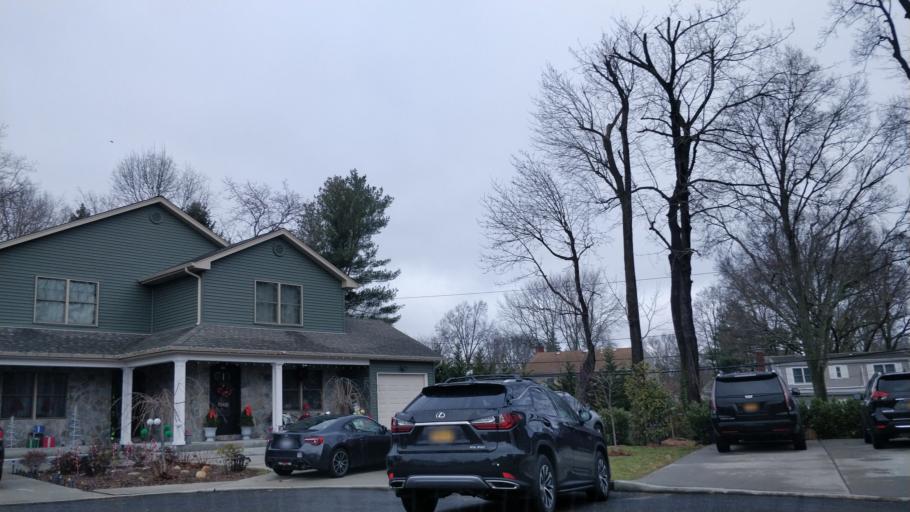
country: US
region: New York
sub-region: Nassau County
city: Locust Valley
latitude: 40.8607
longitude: -73.6094
